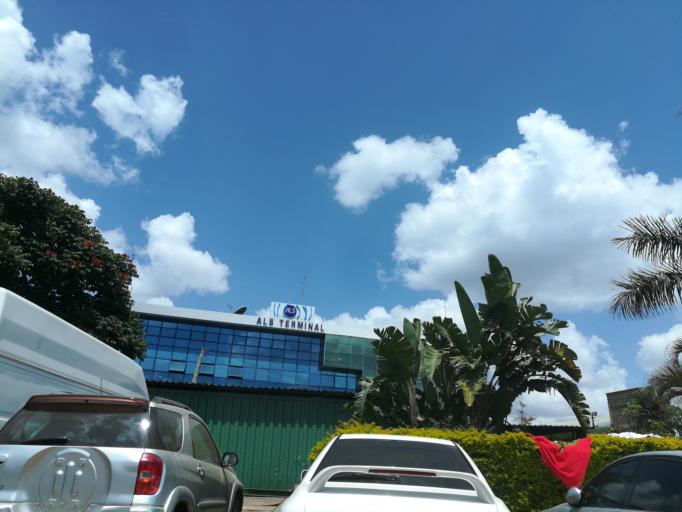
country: KE
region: Nairobi Area
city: Nairobi
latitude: -1.3230
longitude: 36.8040
